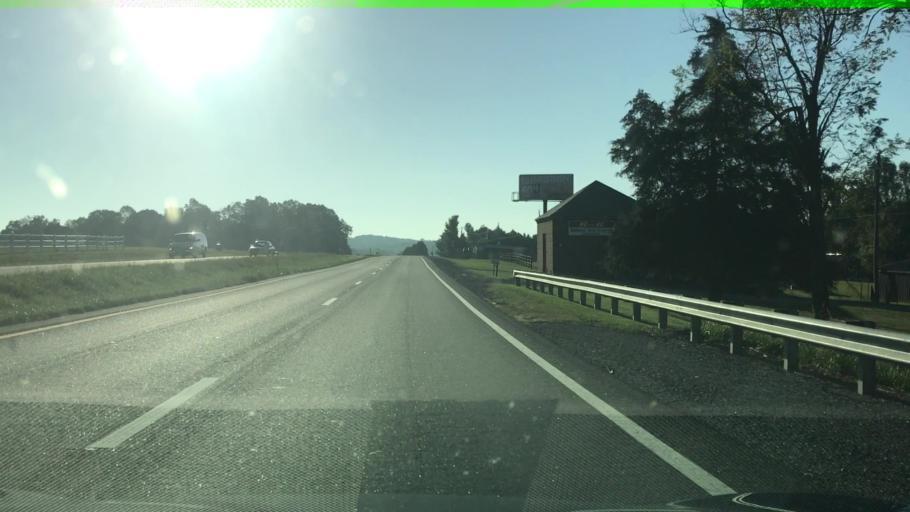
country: US
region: Virginia
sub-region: City of Bedford
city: Bedford
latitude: 37.3144
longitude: -79.4086
